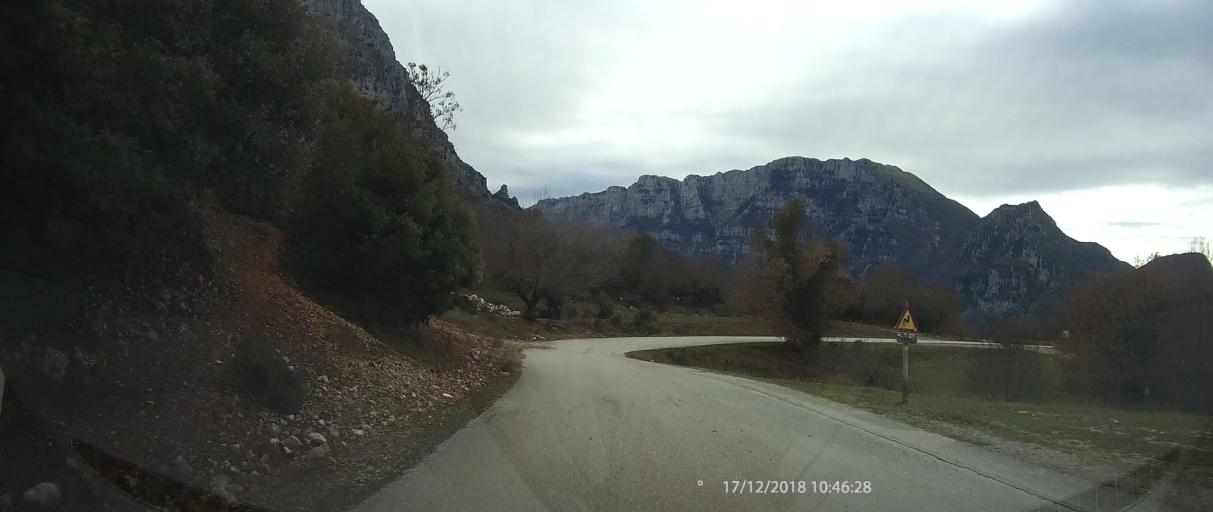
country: GR
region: Epirus
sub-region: Nomos Ioanninon
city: Konitsa
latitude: 39.9639
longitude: 20.7141
